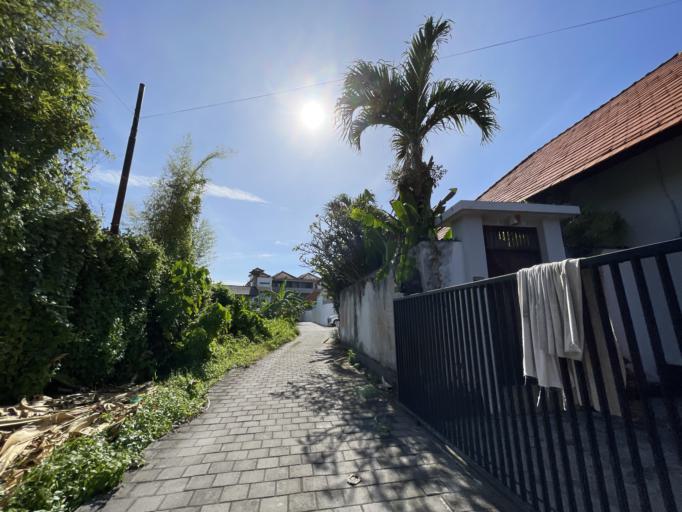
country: ID
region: Bali
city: Kuta
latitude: -8.6761
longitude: 115.1681
